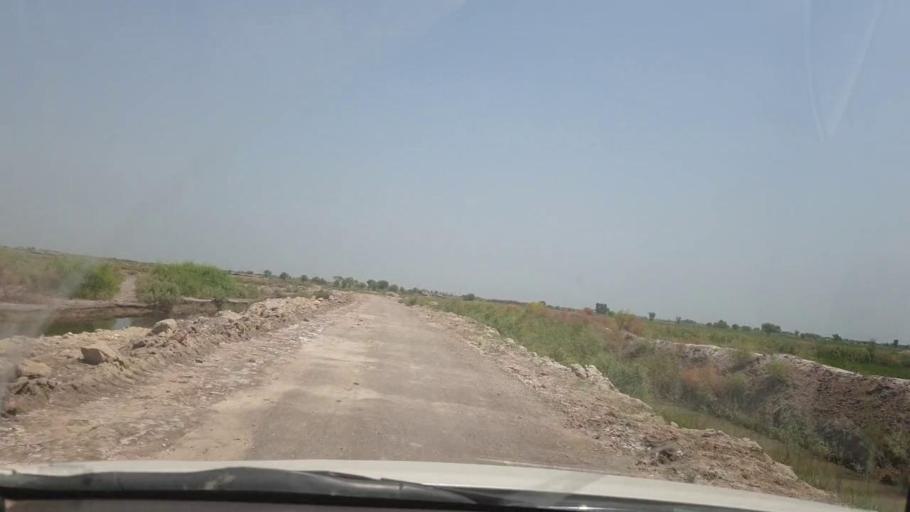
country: PK
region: Sindh
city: Lakhi
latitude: 27.8873
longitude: 68.7461
